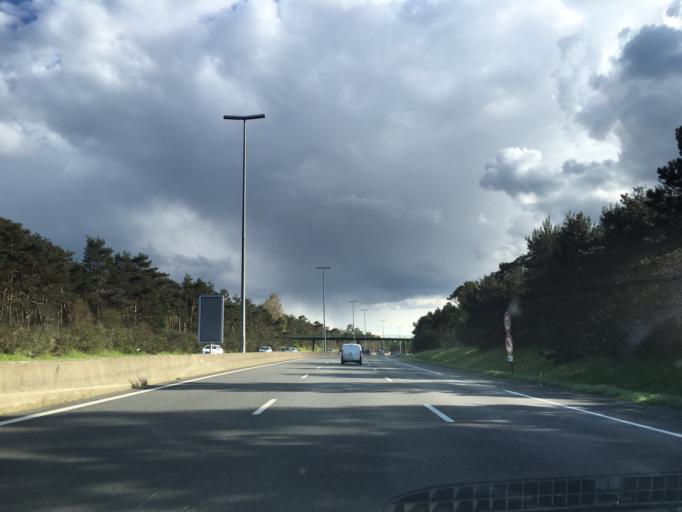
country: FR
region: Picardie
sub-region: Departement de l'Oise
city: Thiers-sur-Theve
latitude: 49.1679
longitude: 2.5993
